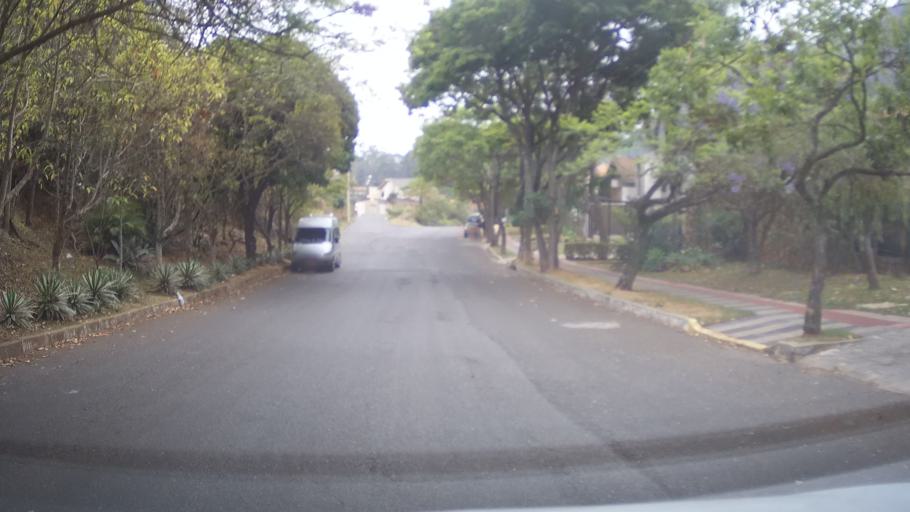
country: BR
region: Minas Gerais
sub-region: Belo Horizonte
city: Belo Horizonte
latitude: -19.9591
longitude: -43.9180
